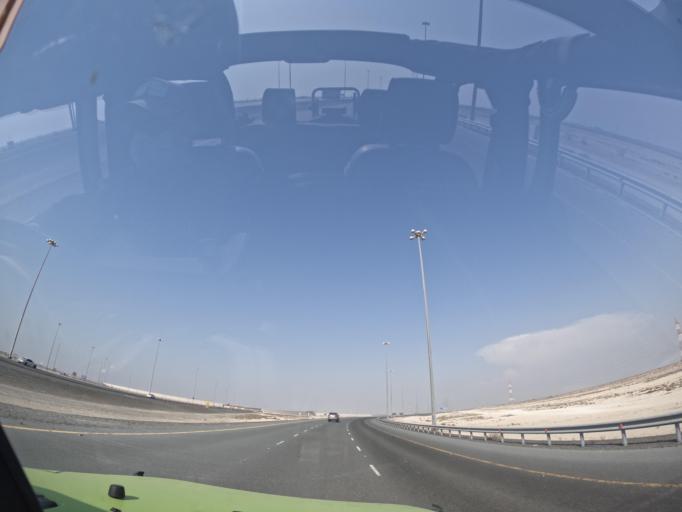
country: AE
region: Abu Dhabi
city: Abu Dhabi
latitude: 24.6693
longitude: 54.8110
